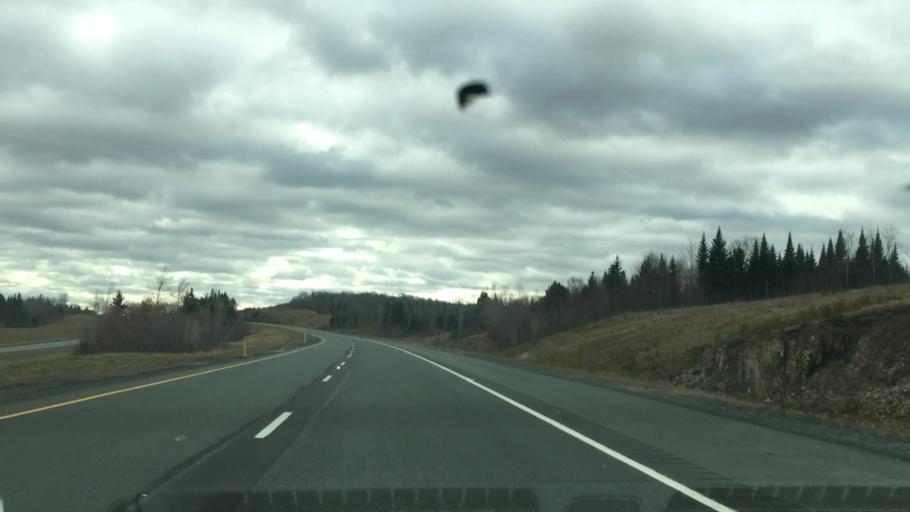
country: US
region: Maine
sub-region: Aroostook County
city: Fort Fairfield
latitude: 46.6414
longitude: -67.7444
